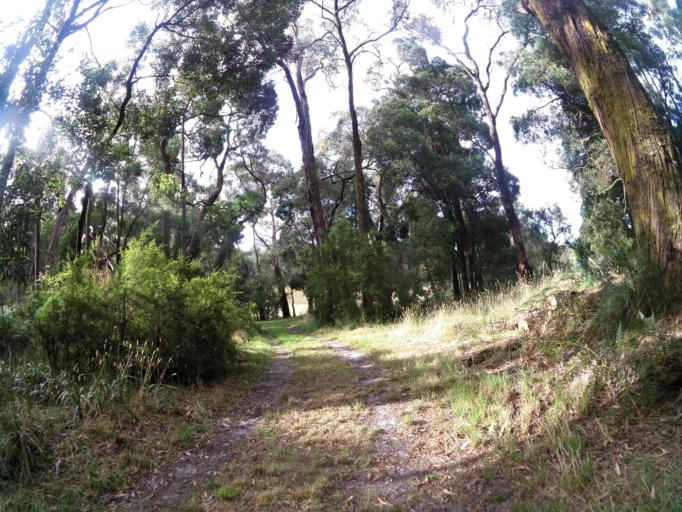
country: AU
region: Victoria
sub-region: Colac-Otway
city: Colac
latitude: -38.5026
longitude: 143.7266
